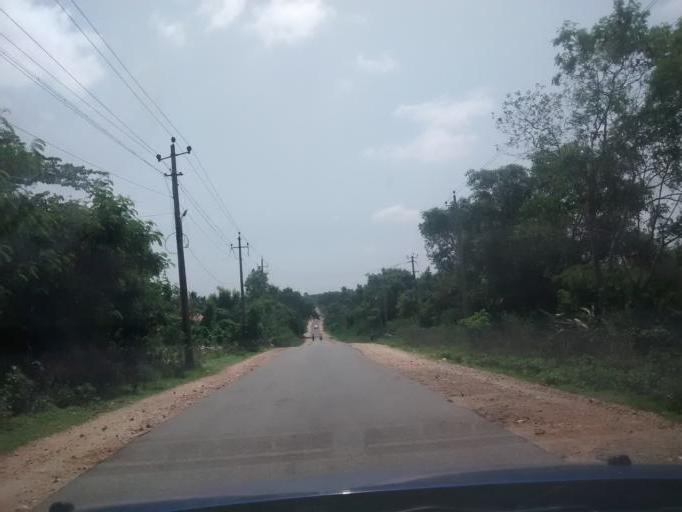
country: IN
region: Karnataka
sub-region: Hassan
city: Hole Narsipur
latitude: 12.5655
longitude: 76.2800
